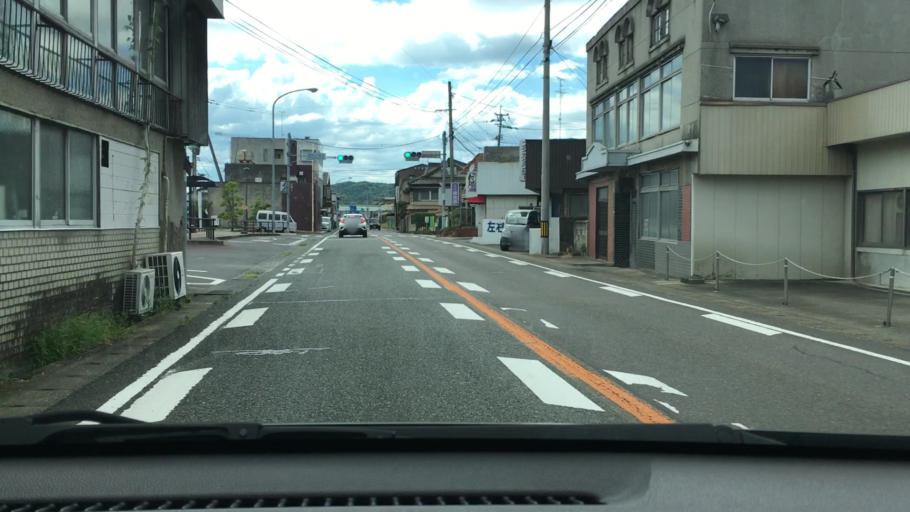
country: JP
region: Saga Prefecture
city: Kashima
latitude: 33.2197
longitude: 130.1613
